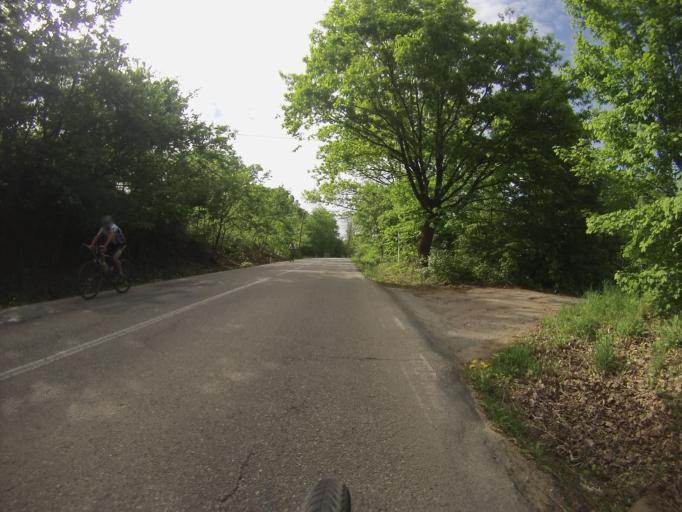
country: CZ
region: South Moravian
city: Kurim
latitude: 49.2397
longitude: 16.5035
